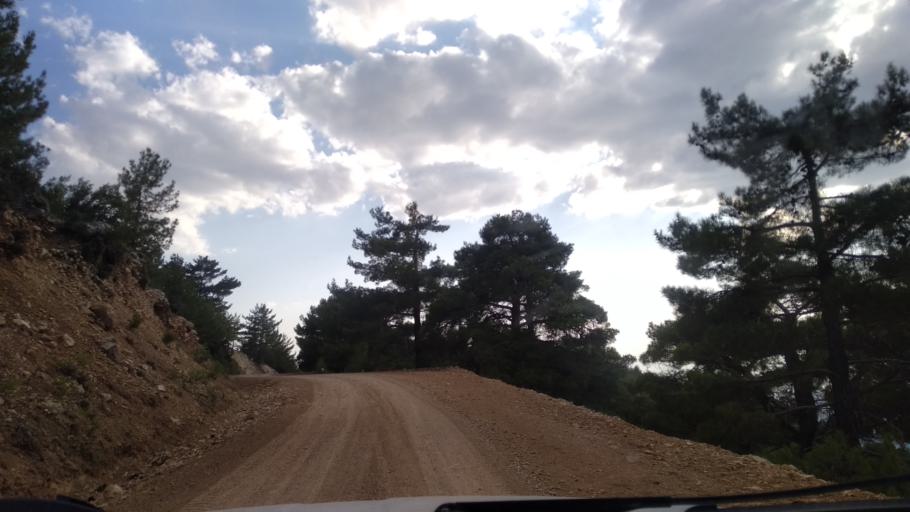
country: TR
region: Mersin
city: Sarikavak
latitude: 36.5950
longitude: 33.6848
